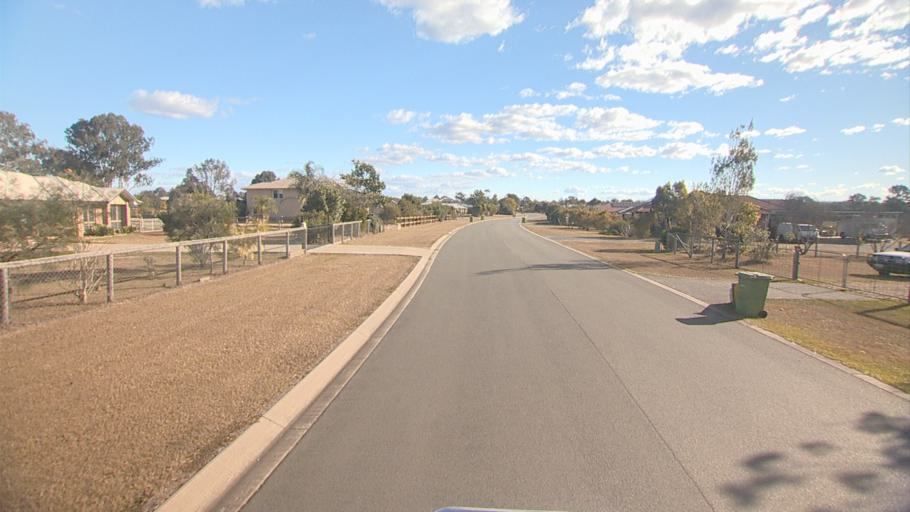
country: AU
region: Queensland
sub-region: Logan
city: North Maclean
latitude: -27.8251
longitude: 153.0060
